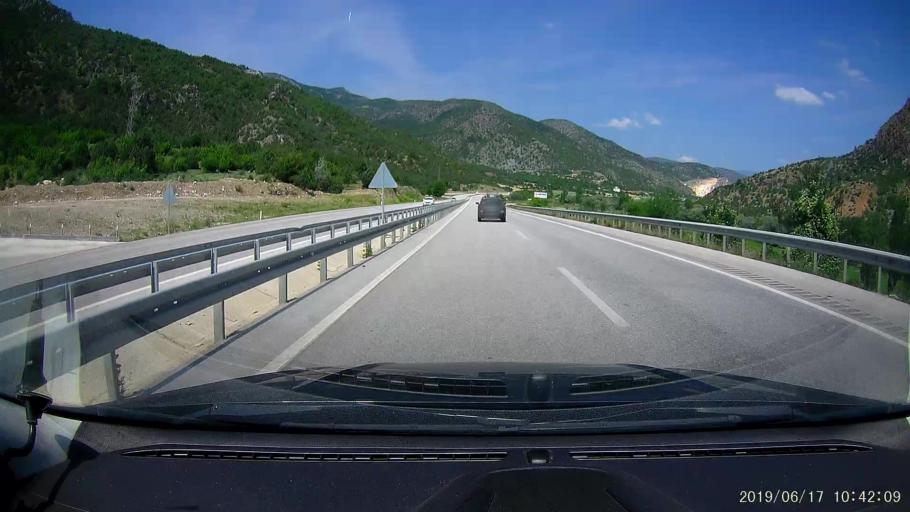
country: TR
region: Corum
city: Kargi
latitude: 41.0465
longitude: 34.5603
